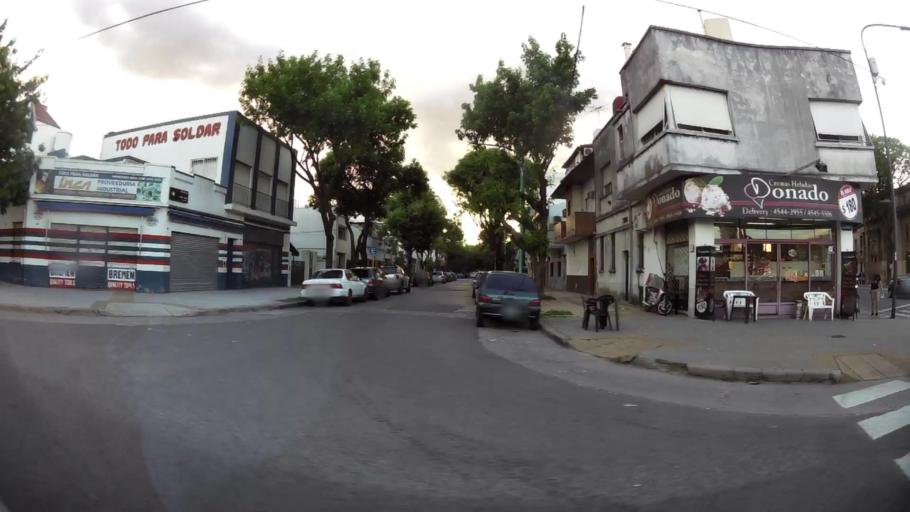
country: AR
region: Buenos Aires
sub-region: Partido de General San Martin
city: General San Martin
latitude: -34.5551
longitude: -58.4887
